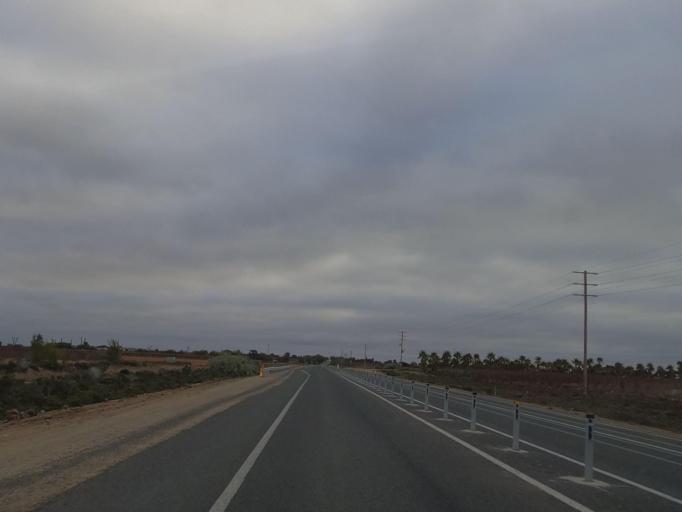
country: AU
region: Victoria
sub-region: Swan Hill
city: Swan Hill
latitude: -35.4722
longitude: 143.6699
